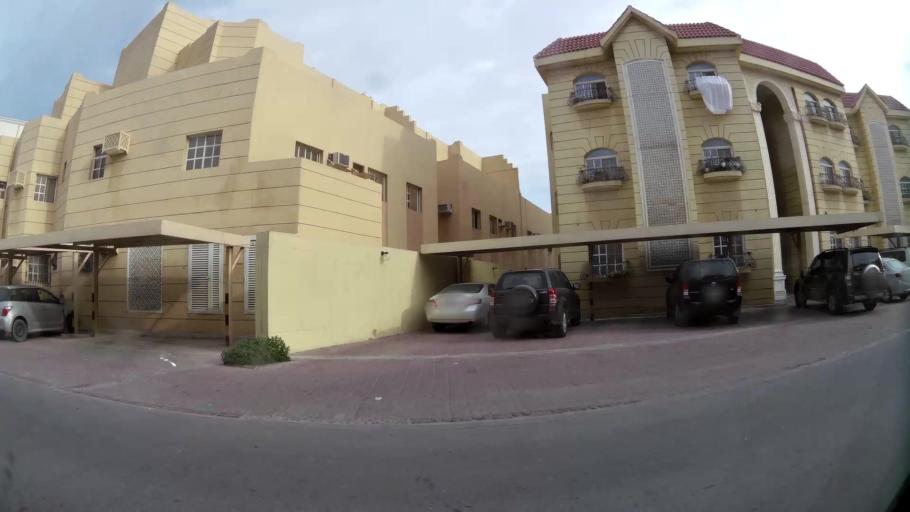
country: QA
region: Baladiyat ad Dawhah
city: Doha
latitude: 25.2788
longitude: 51.4946
